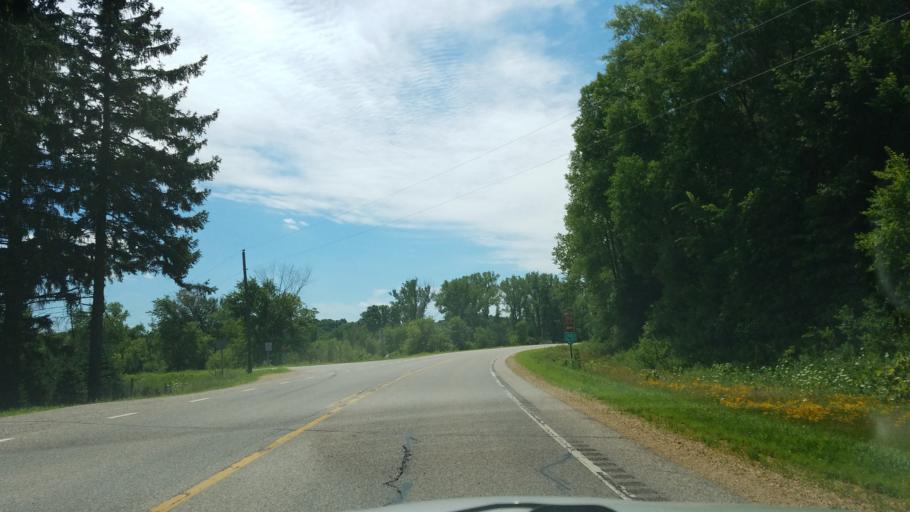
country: US
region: Wisconsin
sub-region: Saint Croix County
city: Glenwood City
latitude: 45.0395
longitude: -92.1770
